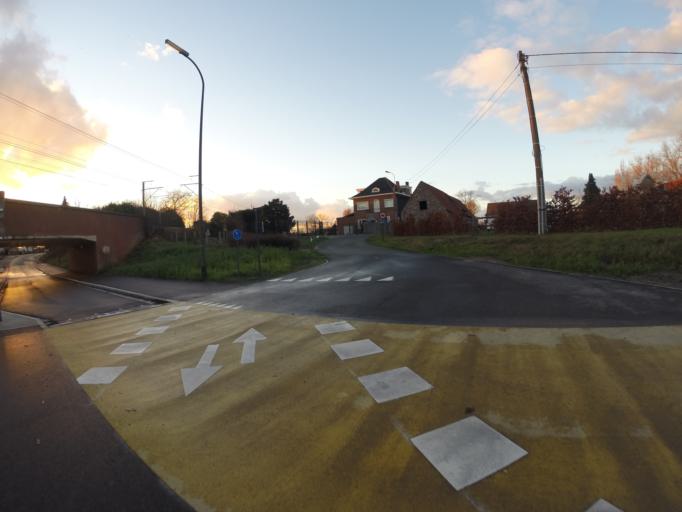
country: BE
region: Flanders
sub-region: Provincie Oost-Vlaanderen
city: Aalter
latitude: 51.0882
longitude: 3.4677
